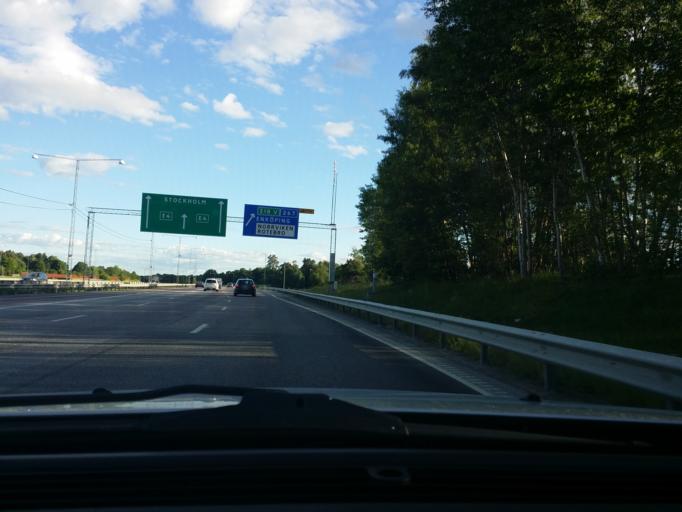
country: SE
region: Stockholm
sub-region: Upplands Vasby Kommun
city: Upplands Vaesby
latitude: 59.4714
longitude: 17.9135
